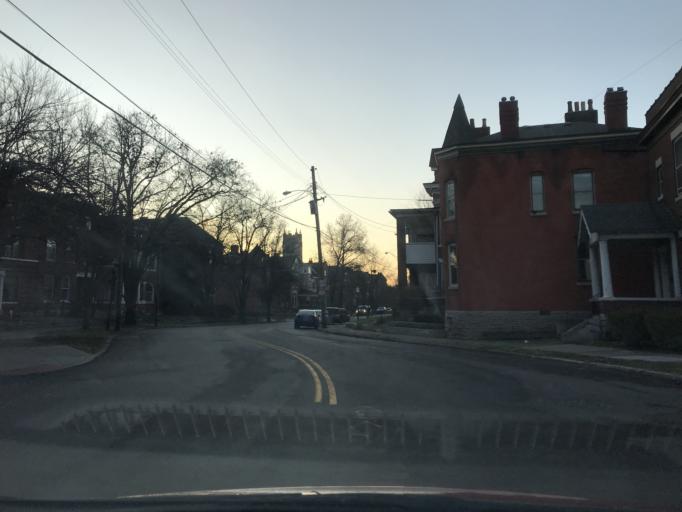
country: US
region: Kentucky
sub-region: Jefferson County
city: Louisville
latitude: 38.2375
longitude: -85.7607
